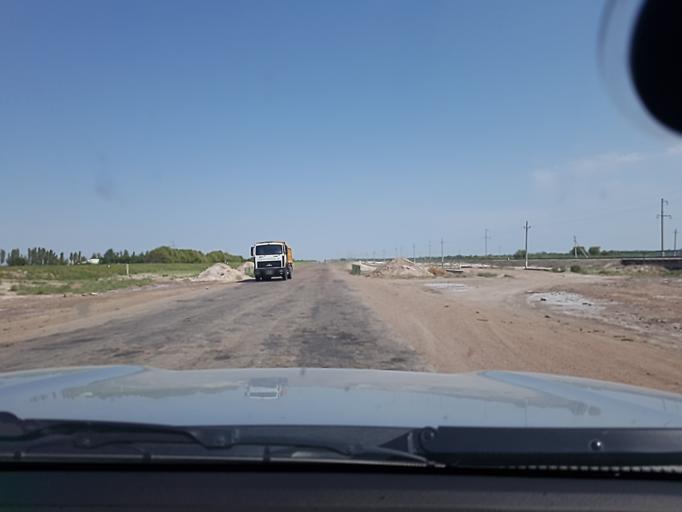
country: TM
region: Dasoguz
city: Koeneuergench
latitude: 42.2613
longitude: 59.3240
